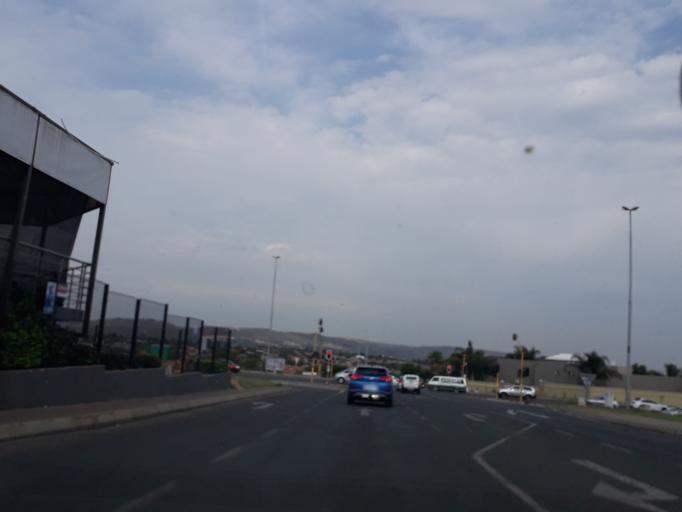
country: ZA
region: Gauteng
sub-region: City of Johannesburg Metropolitan Municipality
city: Roodepoort
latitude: -26.0955
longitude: 27.9277
